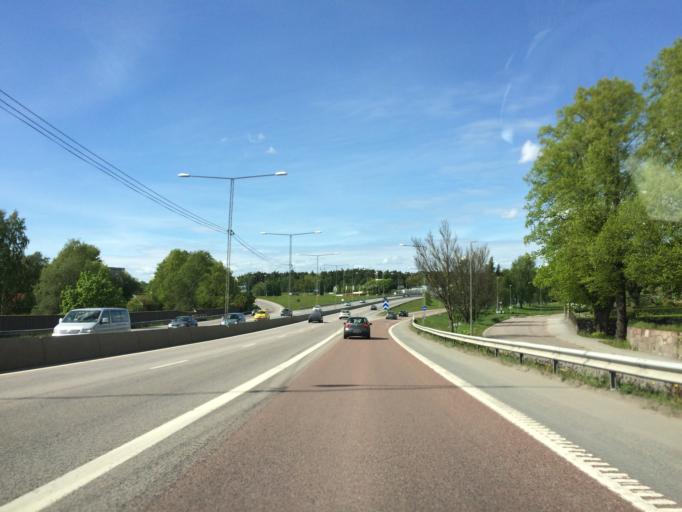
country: SE
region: Stockholm
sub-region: Danderyds Kommun
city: Djursholm
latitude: 59.4064
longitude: 18.0362
